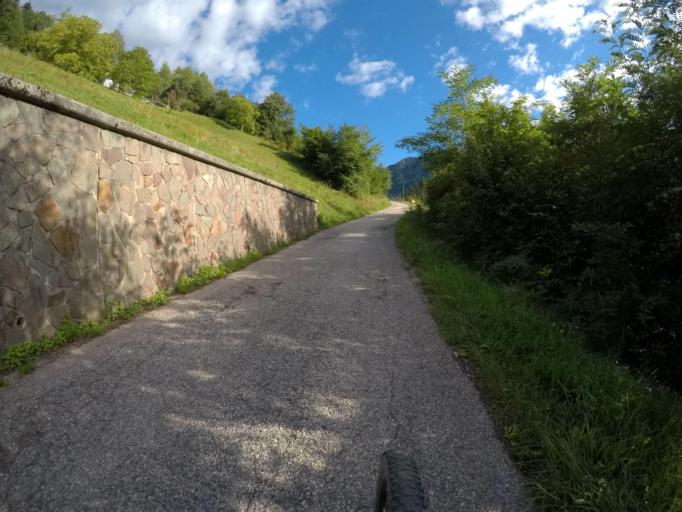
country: IT
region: Friuli Venezia Giulia
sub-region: Provincia di Udine
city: Paularo
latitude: 46.5399
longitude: 13.1134
